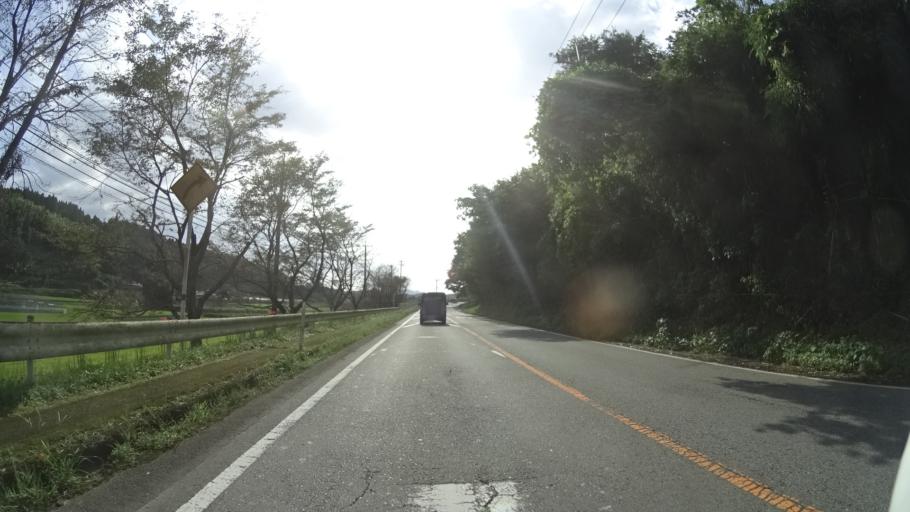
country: JP
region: Kumamoto
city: Ozu
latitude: 32.6800
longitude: 131.0160
